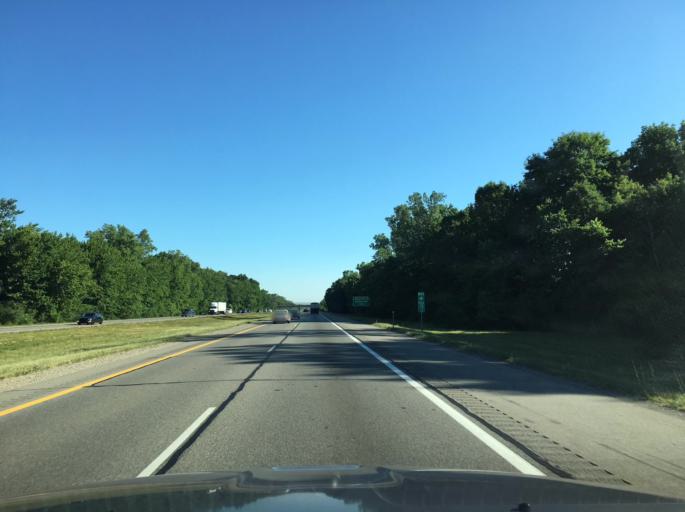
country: US
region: Michigan
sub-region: Macomb County
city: Shelby
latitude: 42.6493
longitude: -83.0139
